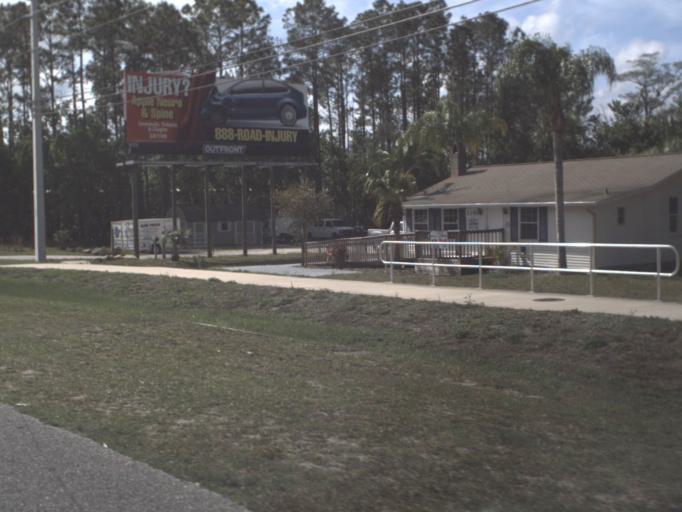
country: US
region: Florida
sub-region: Flagler County
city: Bunnell
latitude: 29.4756
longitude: -81.2368
